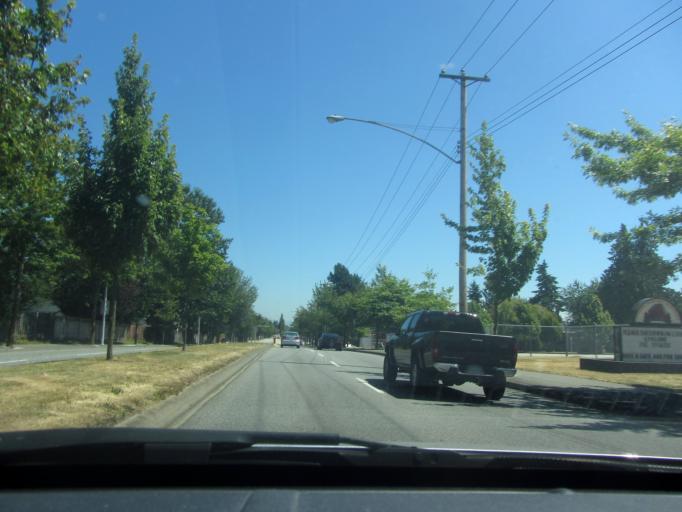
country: CA
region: British Columbia
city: Delta
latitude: 49.1338
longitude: -122.8658
